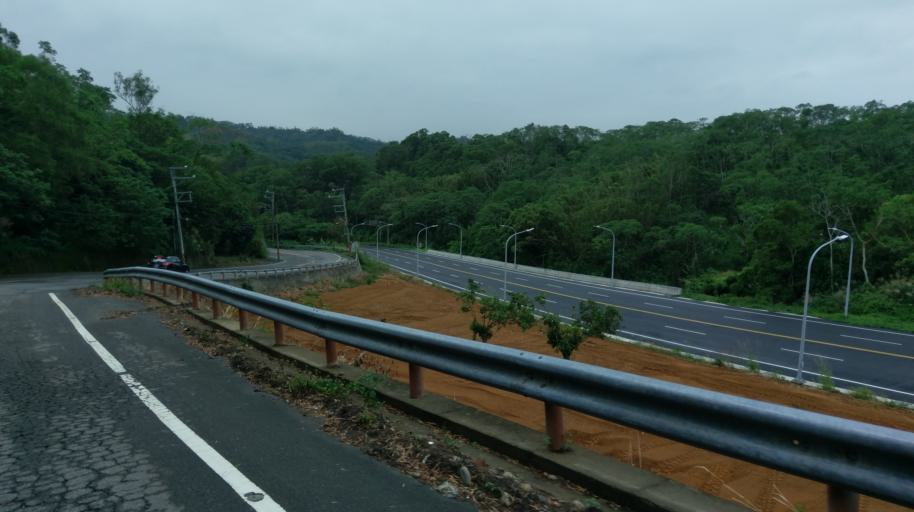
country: TW
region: Taiwan
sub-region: Hsinchu
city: Hsinchu
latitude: 24.7357
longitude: 120.9644
